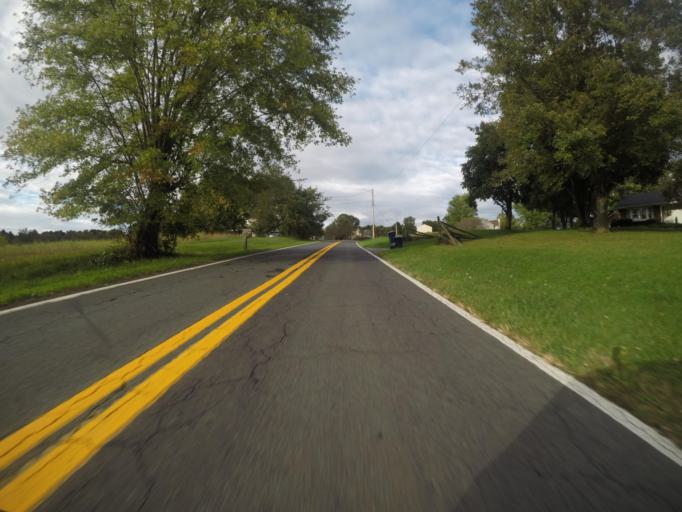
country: US
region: Maryland
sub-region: Carroll County
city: Hampstead
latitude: 39.5581
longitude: -76.8647
